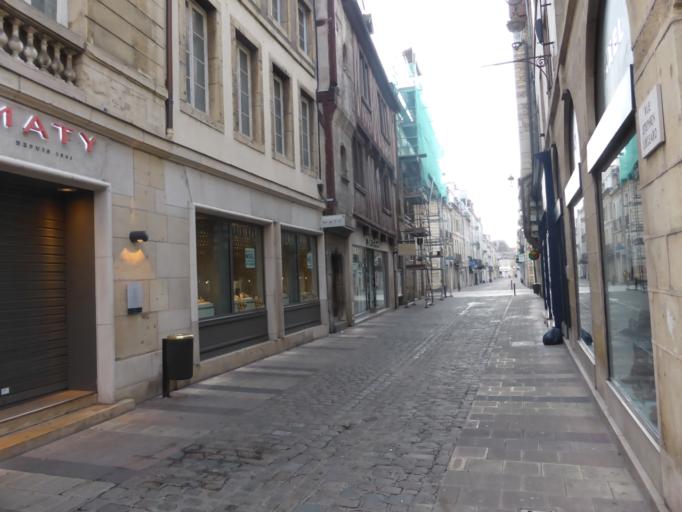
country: FR
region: Bourgogne
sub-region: Departement de la Cote-d'Or
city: Dijon
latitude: 47.3222
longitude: 5.0394
